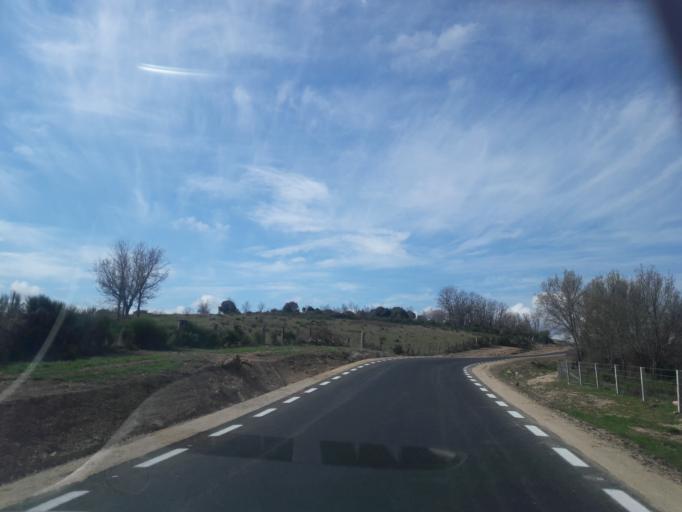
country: ES
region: Castille and Leon
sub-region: Provincia de Salamanca
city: Monleon
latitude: 40.5283
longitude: -5.8352
